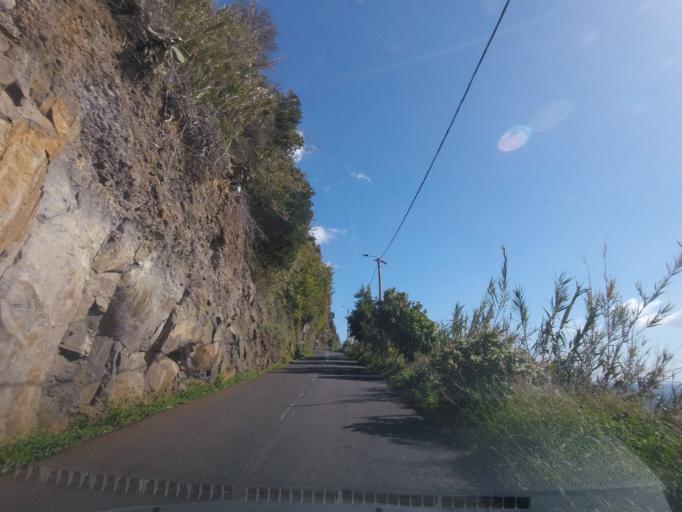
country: PT
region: Madeira
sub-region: Calheta
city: Estreito da Calheta
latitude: 32.7338
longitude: -17.2045
